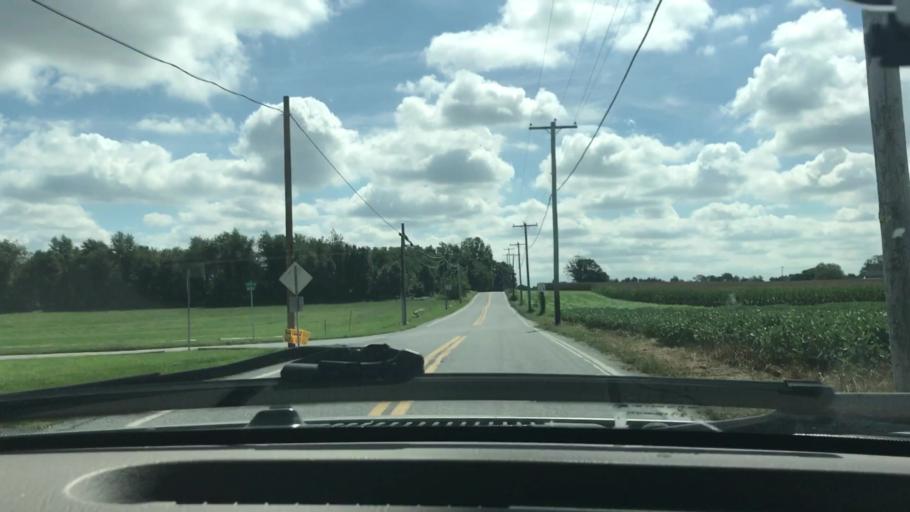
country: US
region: Pennsylvania
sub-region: Lancaster County
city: East Petersburg
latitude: 40.1167
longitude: -76.3795
